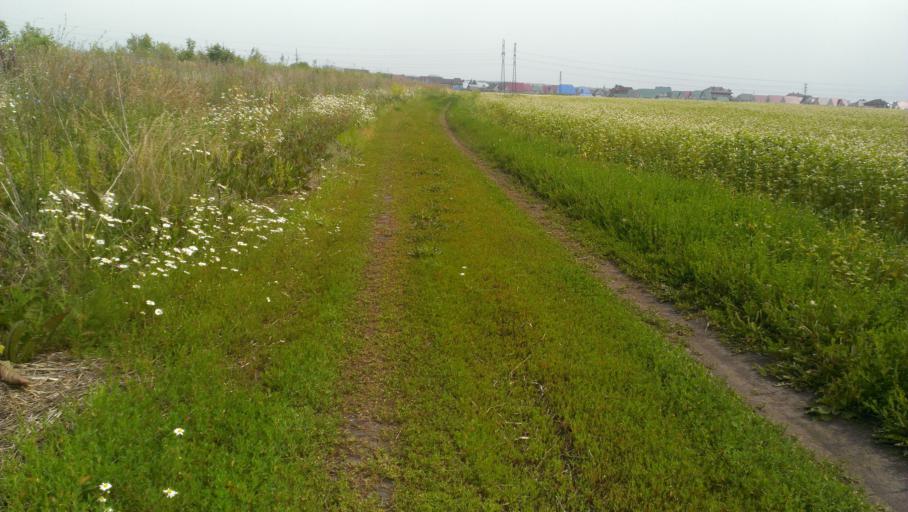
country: RU
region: Altai Krai
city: Novosilikatnyy
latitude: 53.3752
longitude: 83.6453
